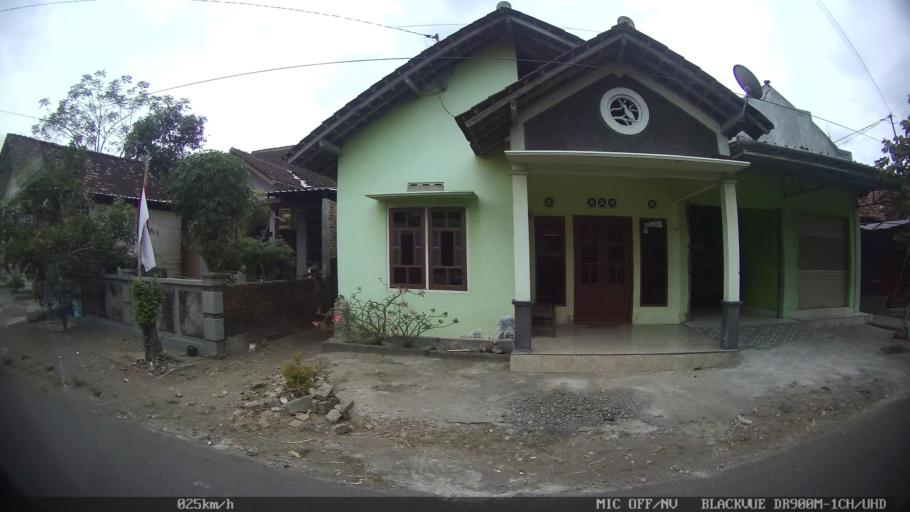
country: ID
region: Daerah Istimewa Yogyakarta
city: Sewon
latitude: -7.8702
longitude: 110.4178
